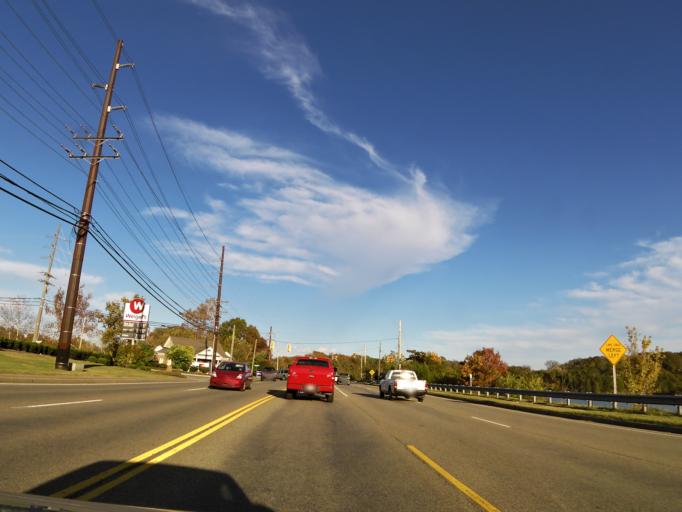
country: US
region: Tennessee
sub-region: Blount County
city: Louisville
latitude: 35.8650
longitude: -84.0619
